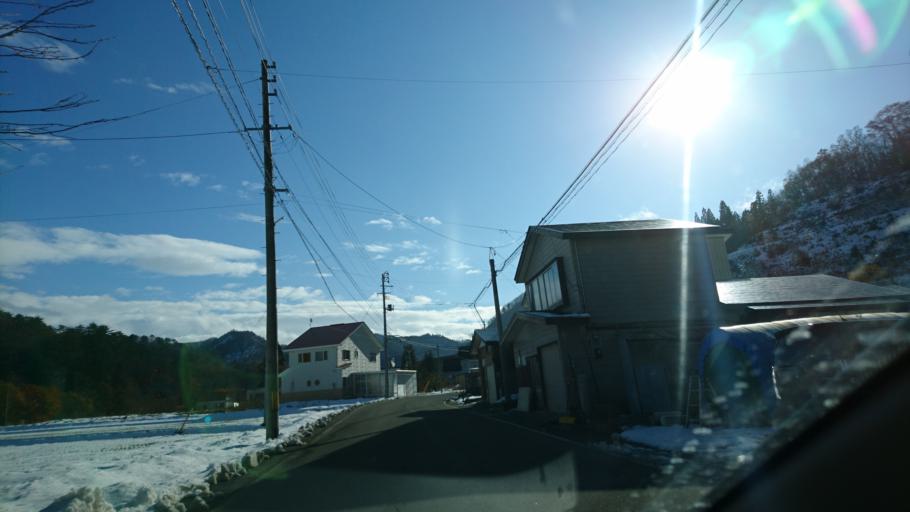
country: JP
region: Akita
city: Yokotemachi
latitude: 39.3096
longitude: 140.7781
